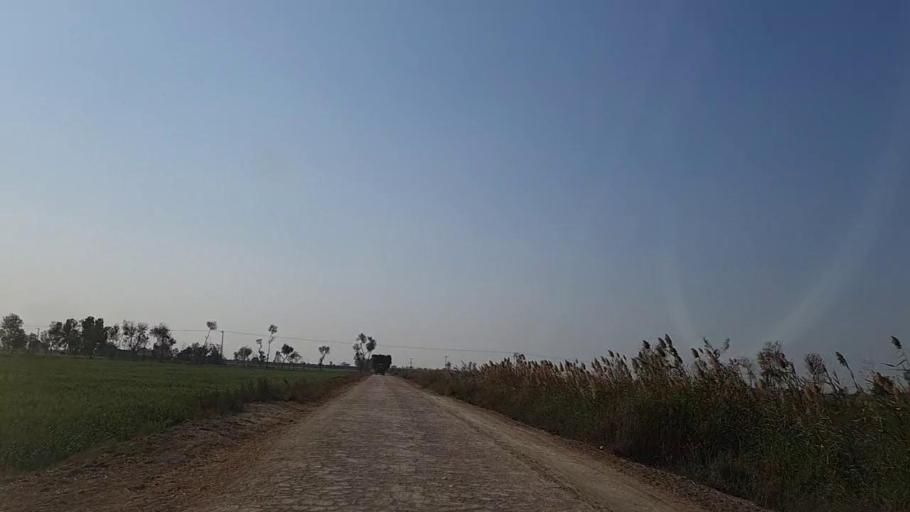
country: PK
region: Sindh
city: Daur
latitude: 26.4713
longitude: 68.3009
